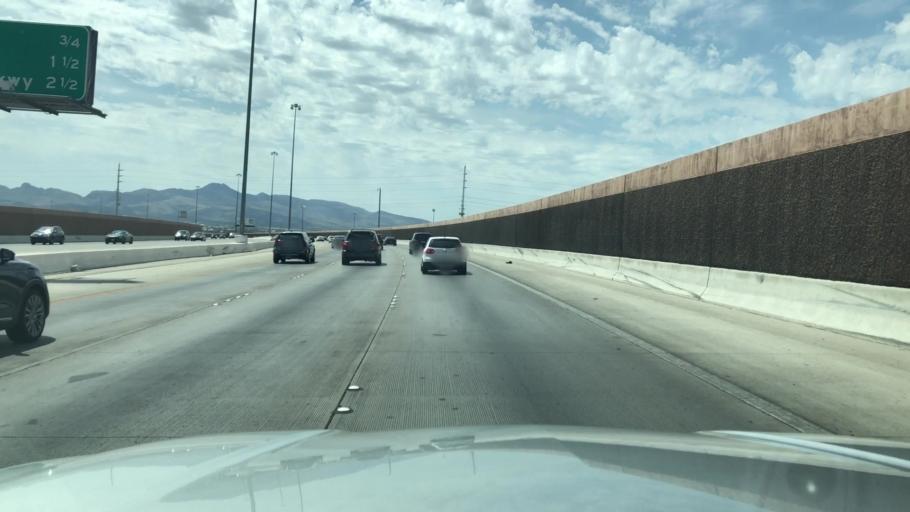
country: US
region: Nevada
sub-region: Clark County
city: Whitney
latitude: 36.0297
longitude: -115.1315
